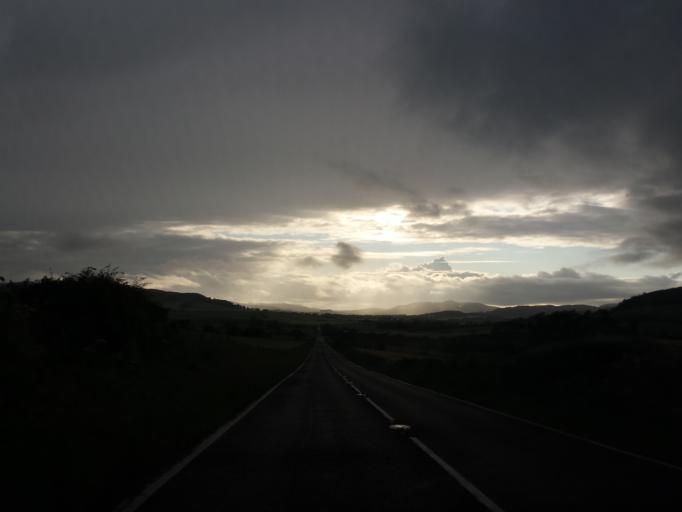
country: GB
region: Scotland
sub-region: Fife
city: Cupar
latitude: 56.3430
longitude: -3.0832
